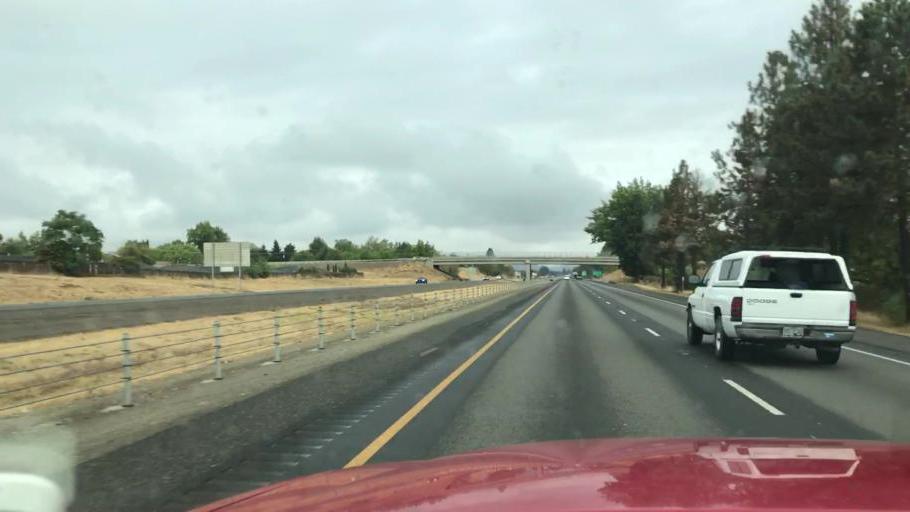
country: US
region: Oregon
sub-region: Jackson County
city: Central Point
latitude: 42.3882
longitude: -122.9168
